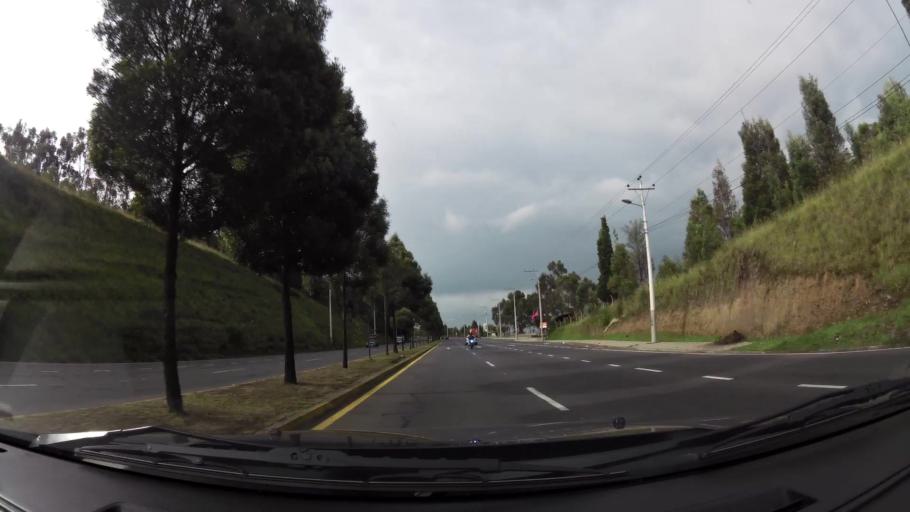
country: EC
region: Pichincha
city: Sangolqui
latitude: -0.3421
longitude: -78.5225
